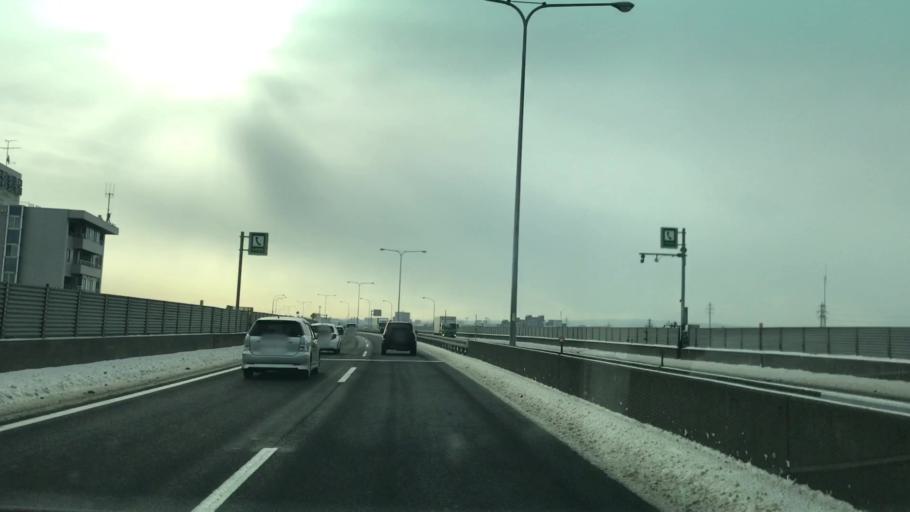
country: JP
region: Hokkaido
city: Sapporo
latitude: 43.0604
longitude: 141.4249
